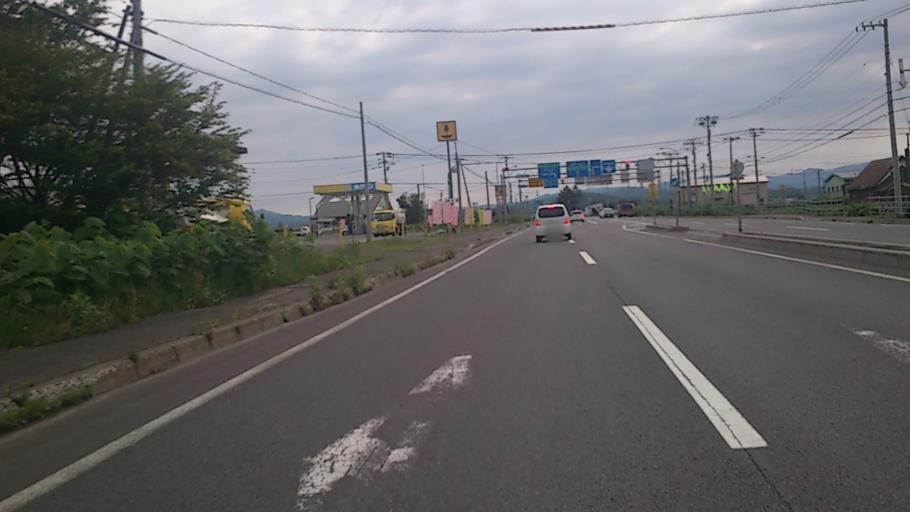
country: JP
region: Hokkaido
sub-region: Asahikawa-shi
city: Asahikawa
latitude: 43.8542
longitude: 142.5039
